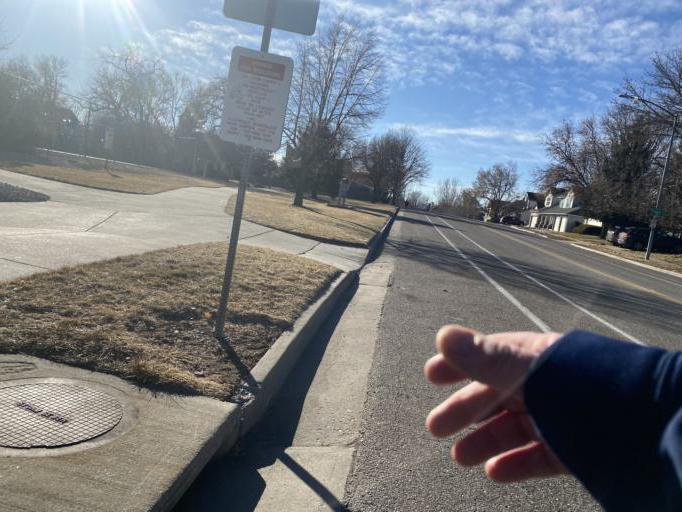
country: US
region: Colorado
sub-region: Jefferson County
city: Applewood
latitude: 39.8091
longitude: -105.1459
